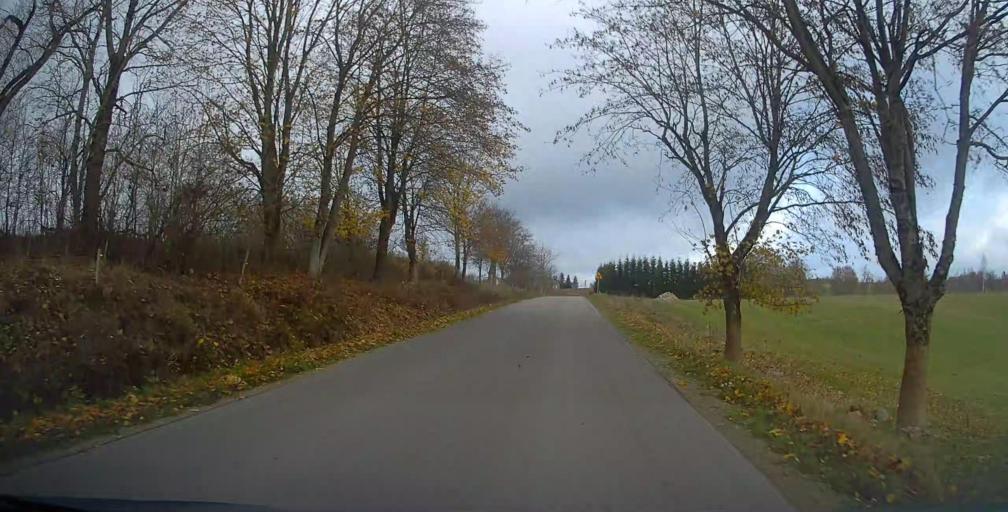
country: PL
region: Podlasie
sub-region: Suwalki
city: Suwalki
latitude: 54.3134
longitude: 22.8786
